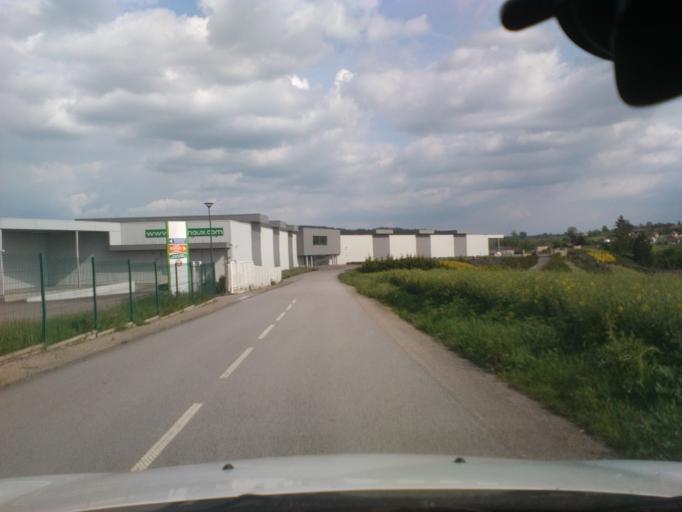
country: FR
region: Lorraine
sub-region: Departement des Vosges
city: Mirecourt
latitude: 48.3311
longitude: 6.1432
